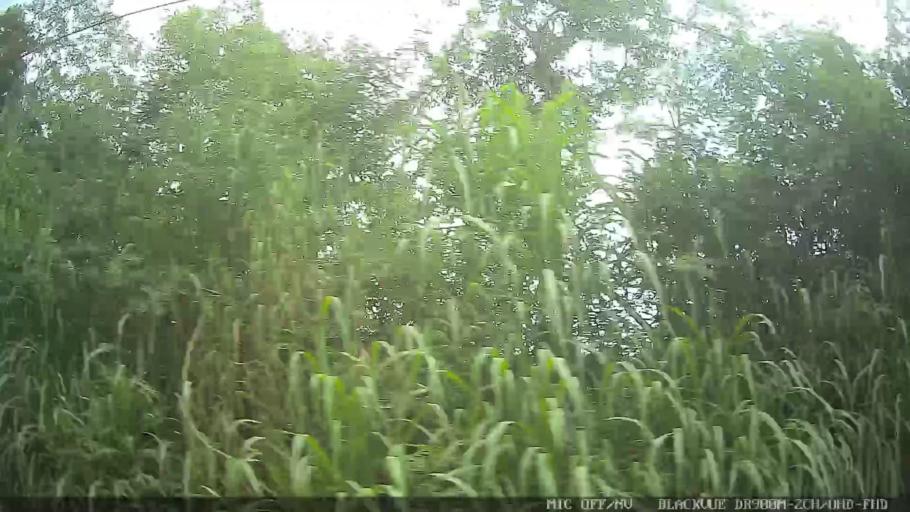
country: BR
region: Sao Paulo
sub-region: Mogi das Cruzes
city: Mogi das Cruzes
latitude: -23.5224
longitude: -46.2313
